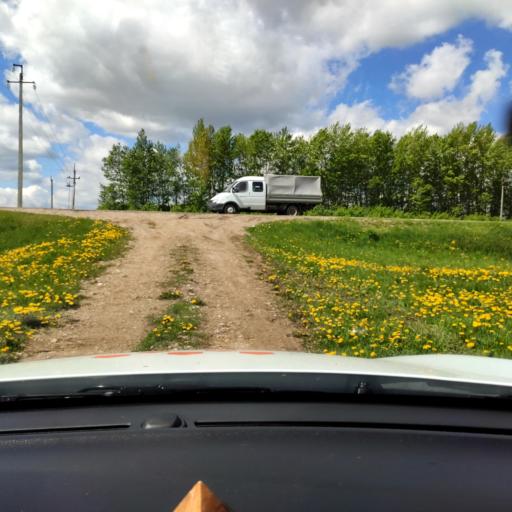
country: RU
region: Tatarstan
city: Kuybyshevskiy Zaton
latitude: 55.2647
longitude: 49.1471
